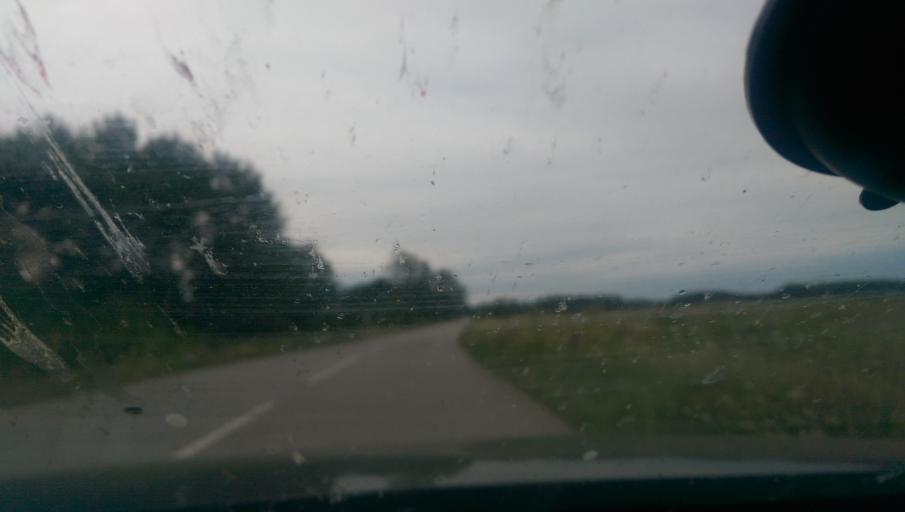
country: LT
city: Priekule
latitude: 55.6187
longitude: 21.3757
